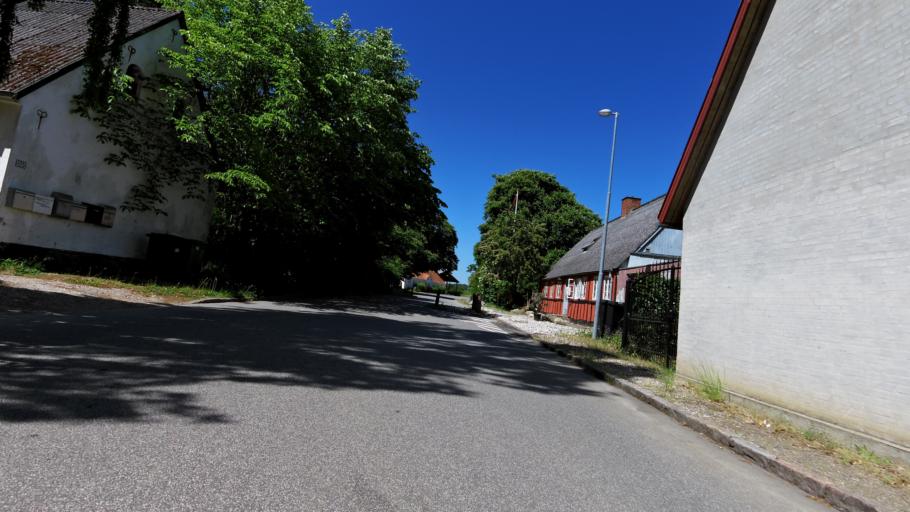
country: DK
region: Central Jutland
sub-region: Arhus Kommune
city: Framlev
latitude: 56.1267
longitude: 9.9895
